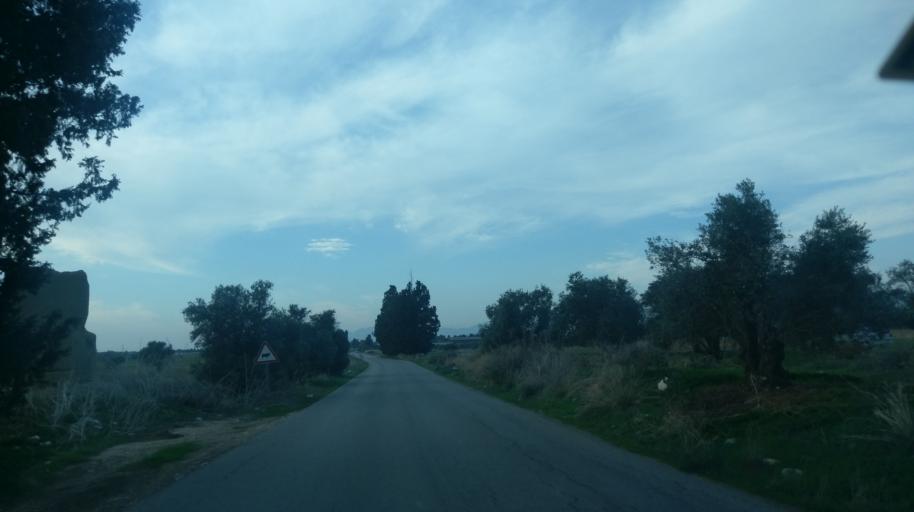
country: CY
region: Larnaka
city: Troulloi
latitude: 35.1491
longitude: 33.6346
